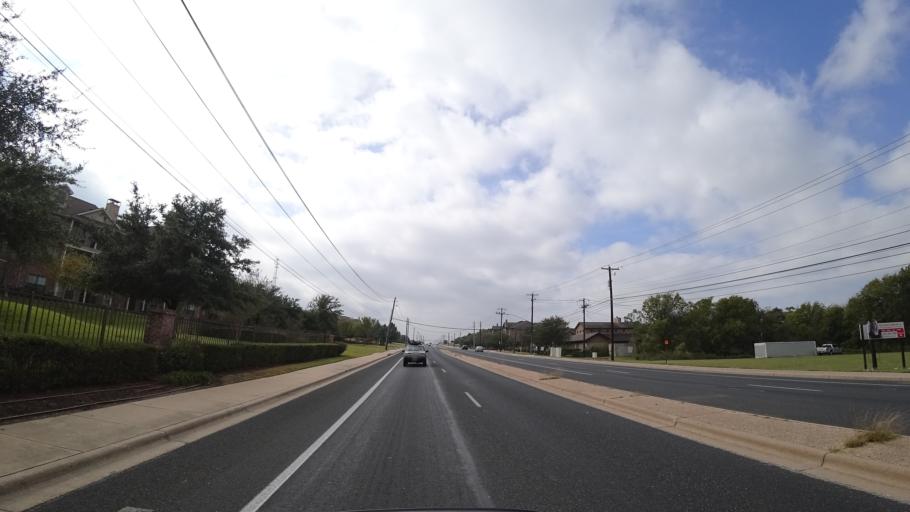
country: US
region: Texas
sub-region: Travis County
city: Shady Hollow
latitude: 30.1995
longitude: -97.8395
